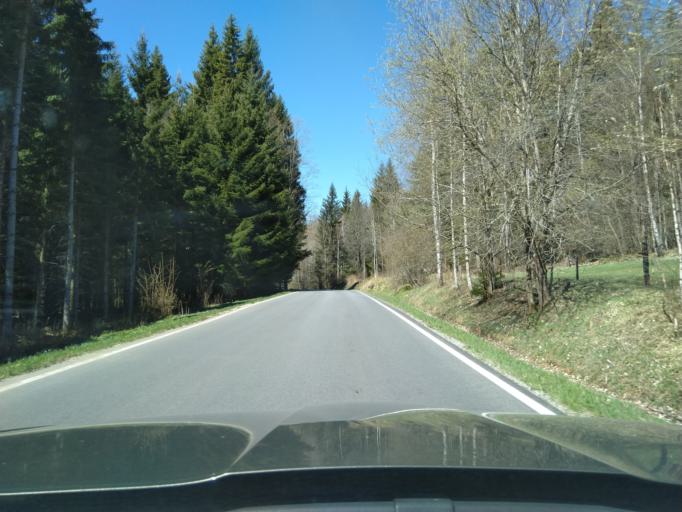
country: CZ
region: Jihocesky
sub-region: Okres Prachatice
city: Vimperk
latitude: 48.9548
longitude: 13.7745
